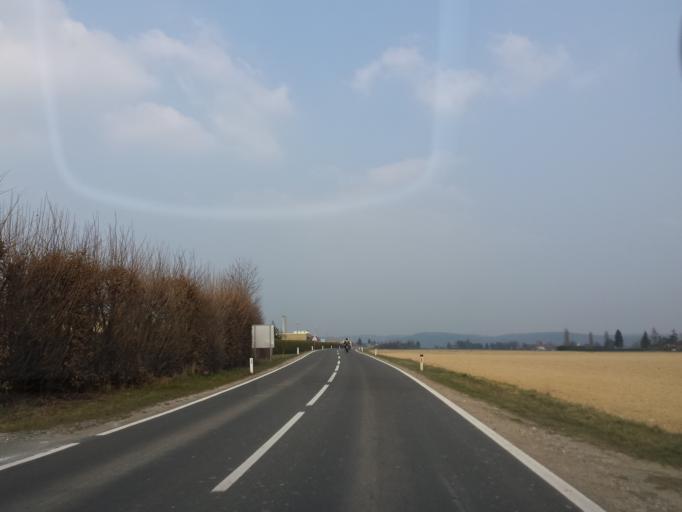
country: AT
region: Styria
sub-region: Politischer Bezirk Hartberg-Fuerstenfeld
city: Fuerstenfeld
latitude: 47.0329
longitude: 16.0890
